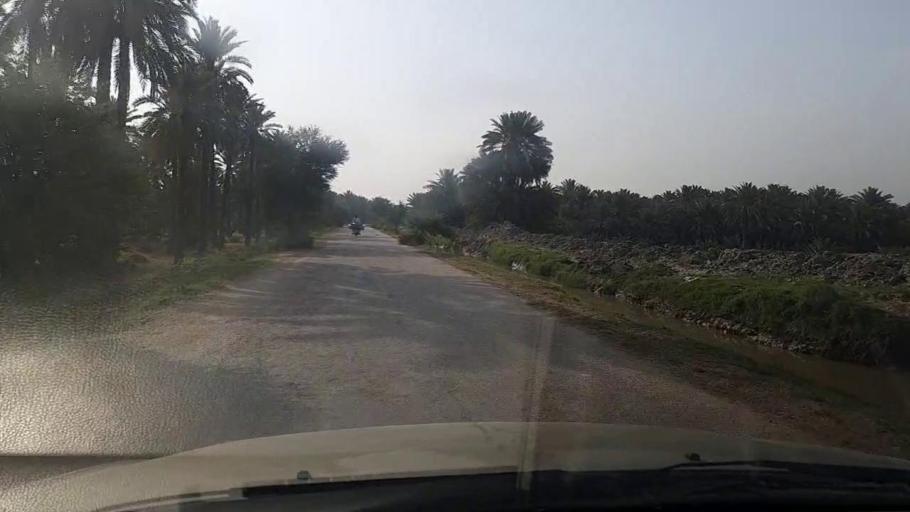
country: PK
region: Sindh
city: Pir jo Goth
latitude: 27.5604
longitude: 68.5441
